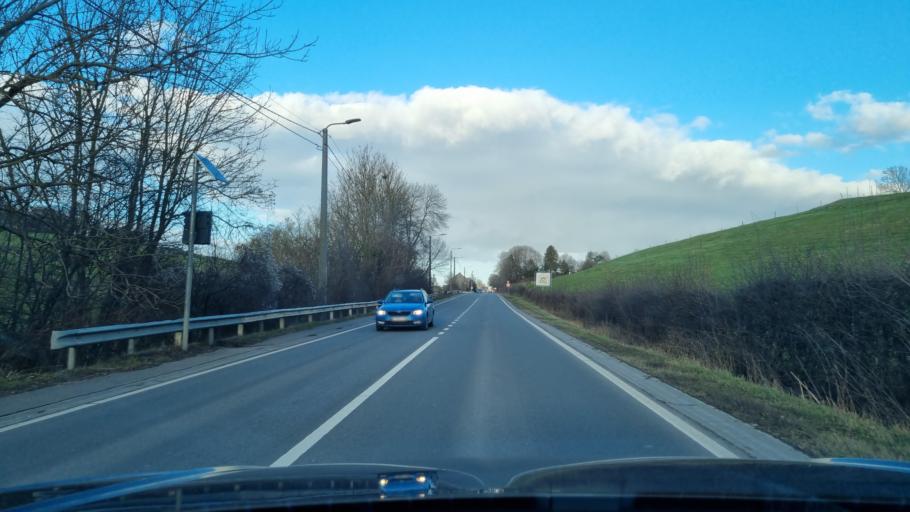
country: BE
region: Wallonia
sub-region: Province de Liege
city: Baelen
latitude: 50.6235
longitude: 5.9604
